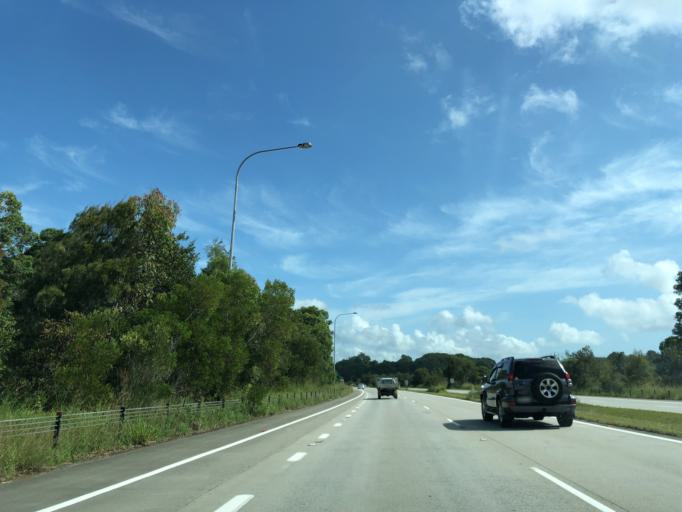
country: AU
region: New South Wales
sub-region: Byron Shire
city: Brunswick Heads
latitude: -28.5803
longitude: 153.5443
